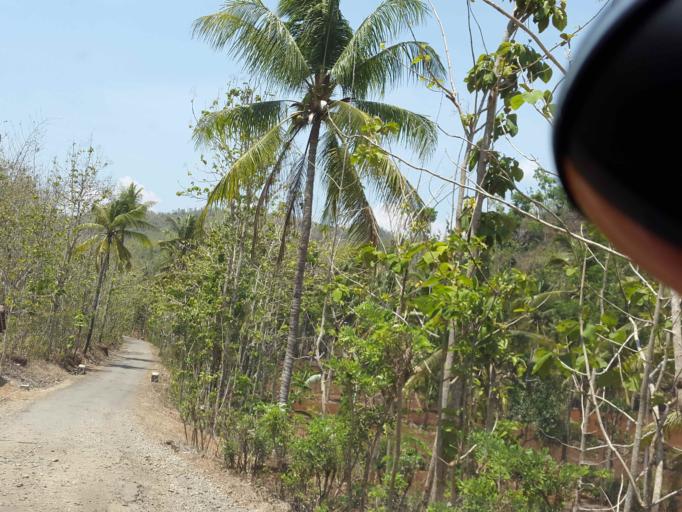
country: ID
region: East Java
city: Krajan
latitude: -8.2033
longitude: 110.9673
